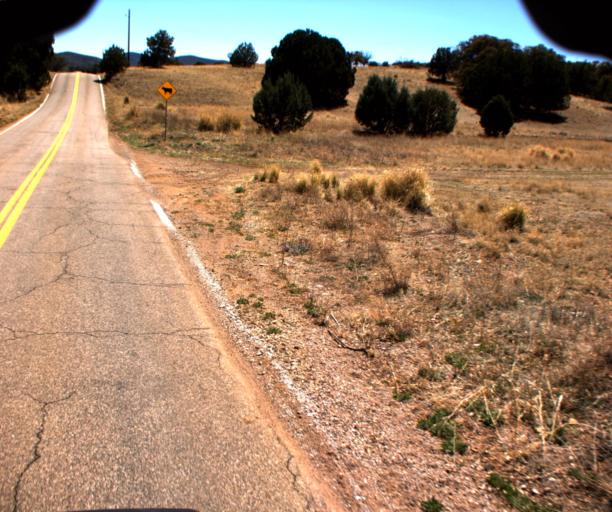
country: US
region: Arizona
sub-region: Cochise County
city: Huachuca City
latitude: 31.5543
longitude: -110.5289
